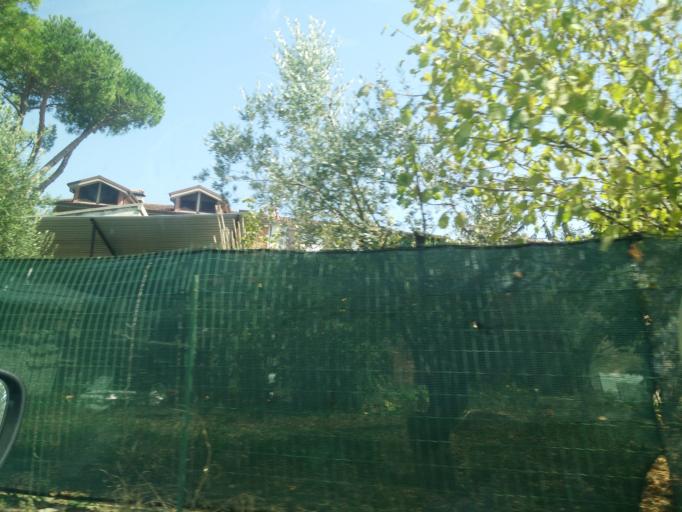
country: IT
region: Tuscany
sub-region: Provincia di Massa-Carrara
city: Carrara
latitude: 44.0582
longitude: 10.0840
